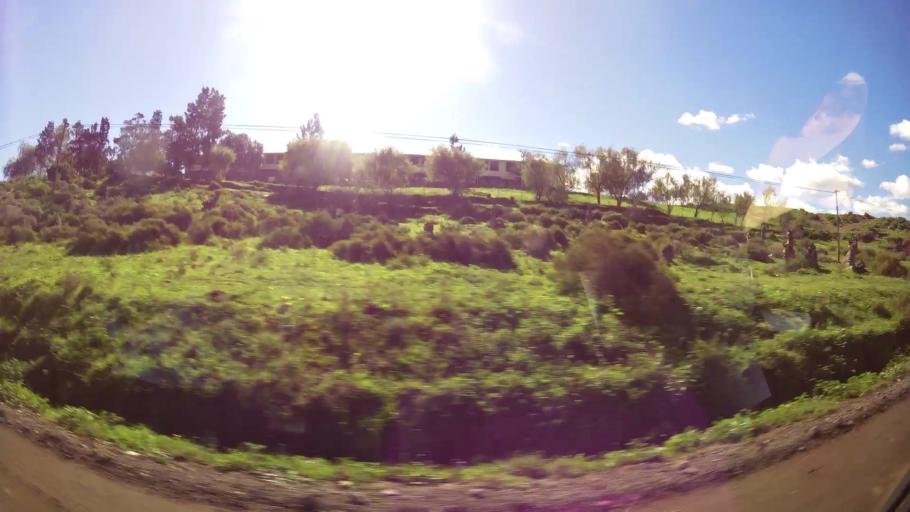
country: ZA
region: Western Cape
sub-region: Cape Winelands District Municipality
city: Ashton
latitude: -33.7939
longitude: 19.8994
